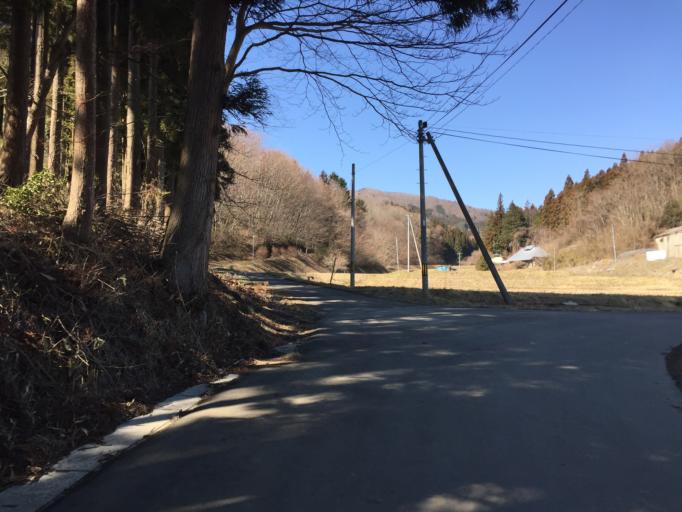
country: JP
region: Fukushima
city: Funehikimachi-funehiki
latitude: 37.3678
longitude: 140.5938
